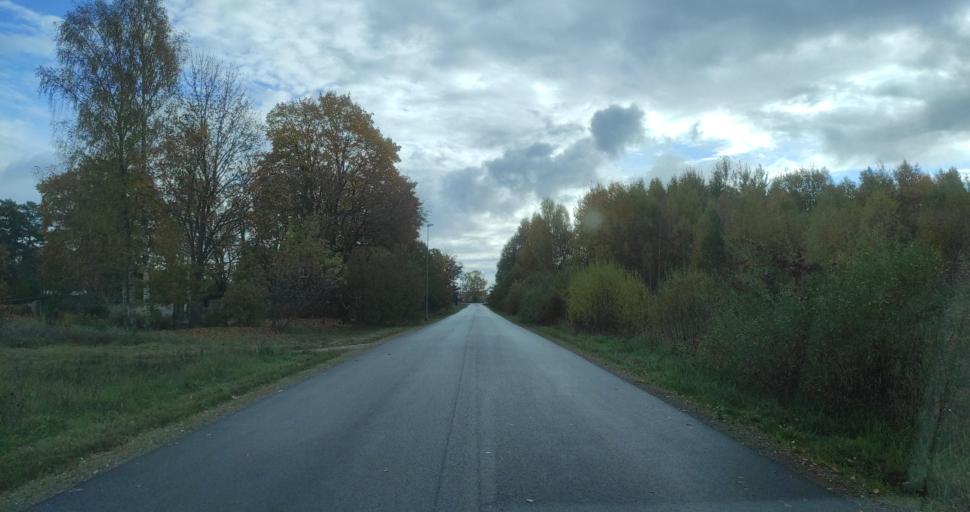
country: LV
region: Skrunda
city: Skrunda
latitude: 56.6839
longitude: 22.0102
